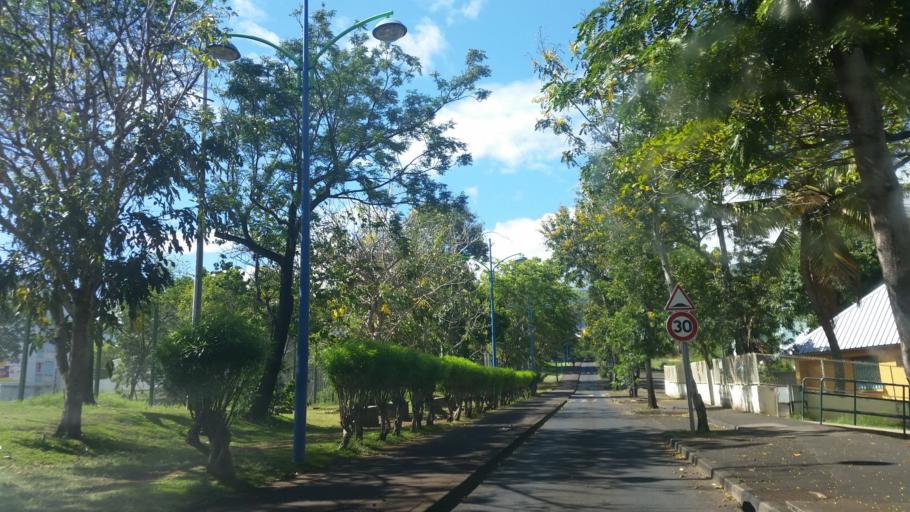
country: RE
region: Reunion
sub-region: Reunion
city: Saint-Denis
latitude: -20.8965
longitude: 55.4864
